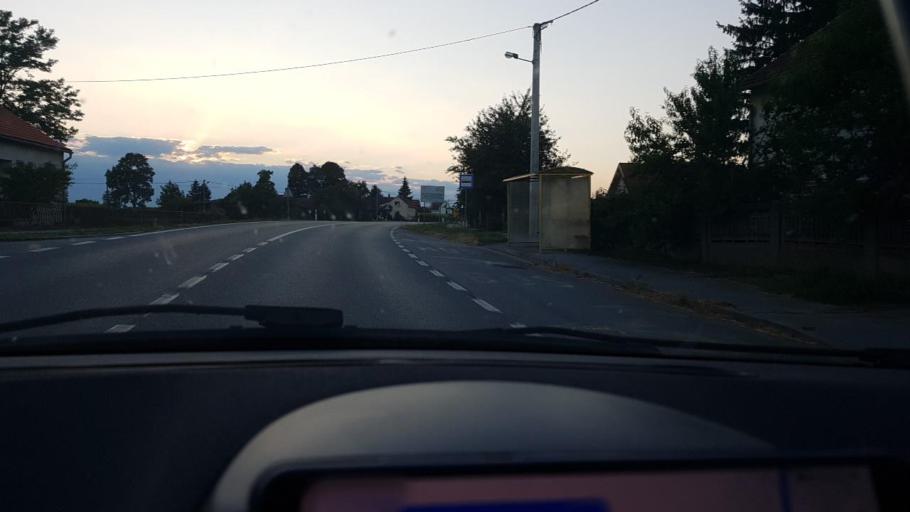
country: HR
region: Bjelovarsko-Bilogorska
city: Zdralovi
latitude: 45.8530
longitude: 16.9306
